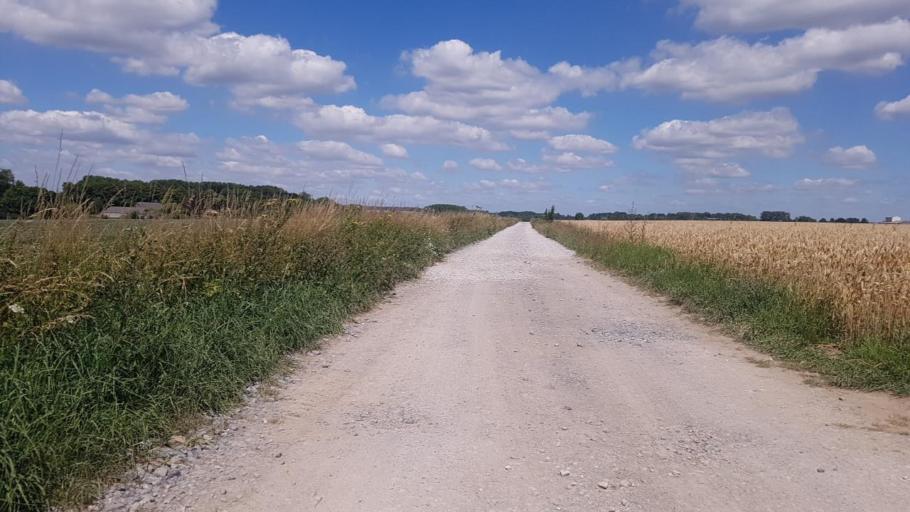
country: BE
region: Wallonia
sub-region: Province du Hainaut
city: Thuin
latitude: 50.3121
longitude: 4.3478
